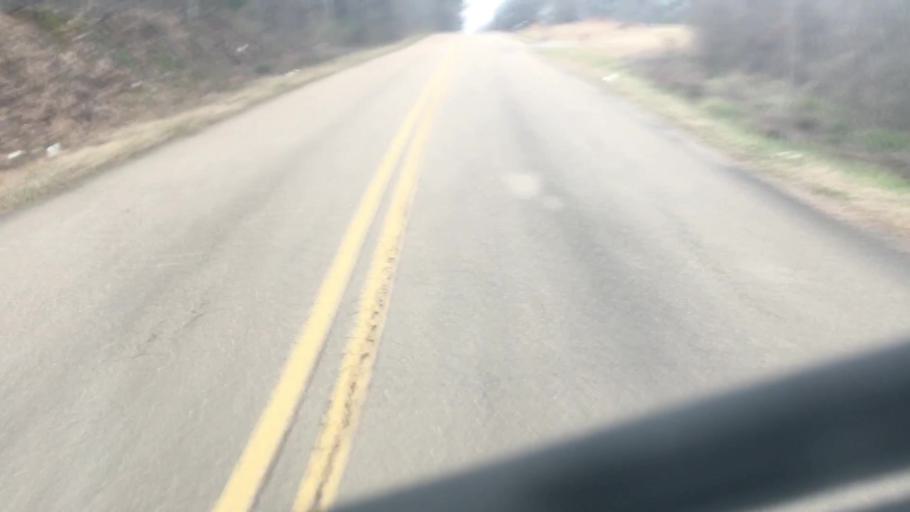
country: US
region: Alabama
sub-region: Walker County
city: Jasper
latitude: 33.8284
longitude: -87.2253
